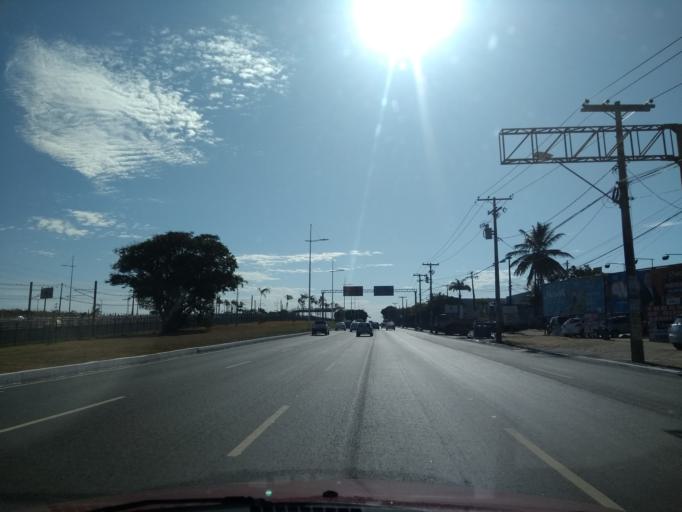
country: BR
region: Bahia
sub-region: Lauro De Freitas
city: Lauro de Freitas
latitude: -12.9222
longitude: -38.3642
